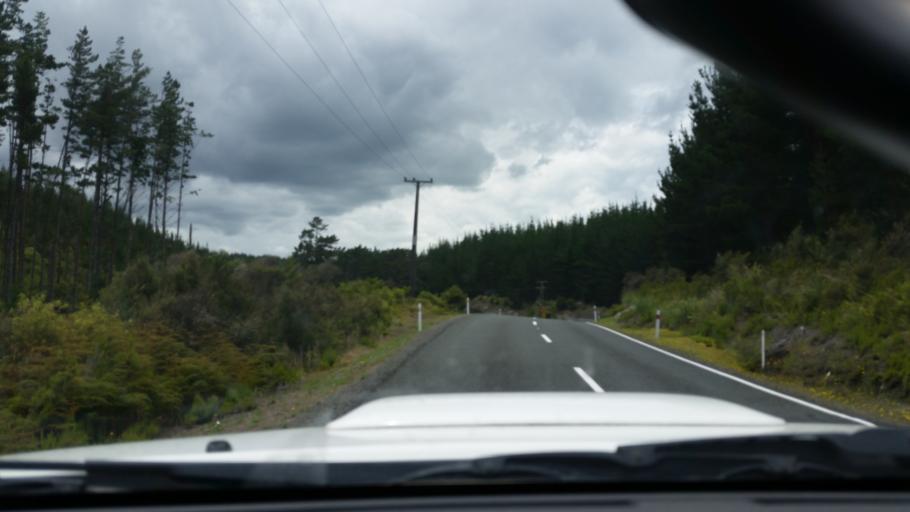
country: NZ
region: Northland
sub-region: Kaipara District
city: Dargaville
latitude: -35.8166
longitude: 173.7155
